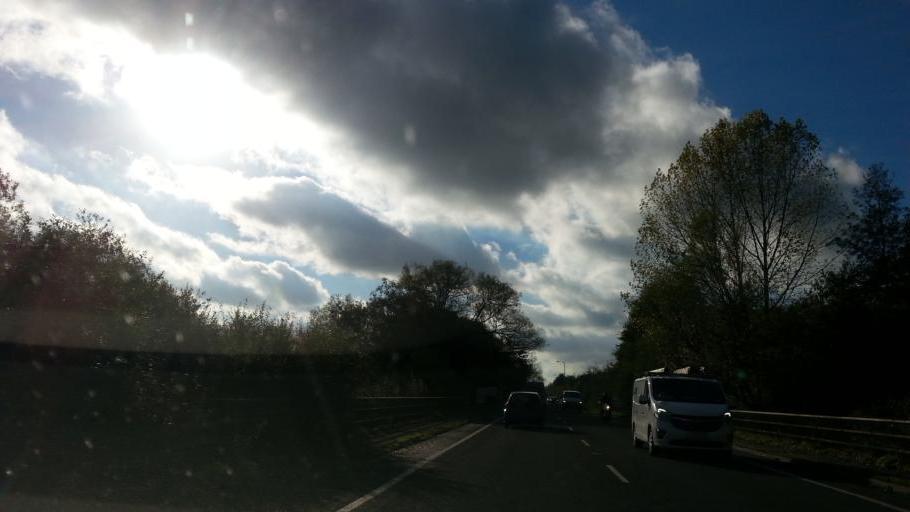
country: GB
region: England
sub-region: Suffolk
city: Bungay
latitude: 52.4611
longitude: 1.4360
